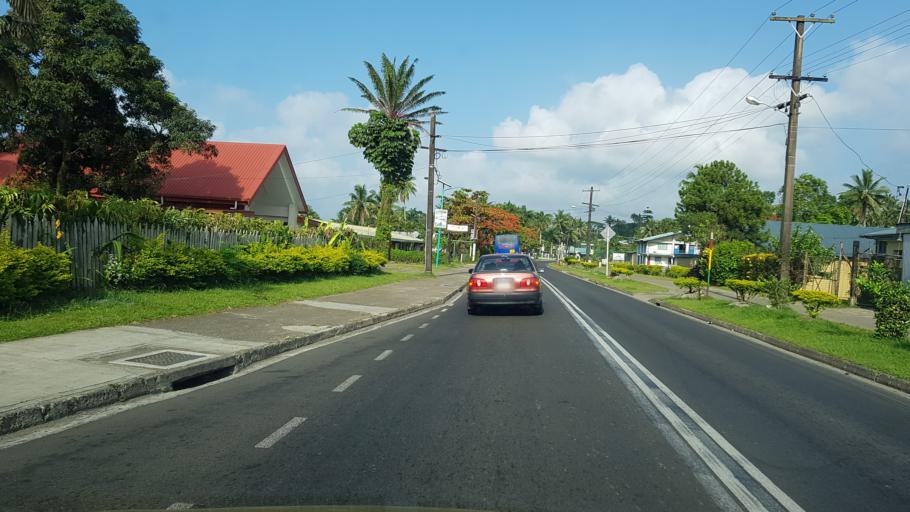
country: FJ
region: Central
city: Suva
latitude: -18.1135
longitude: 178.4060
